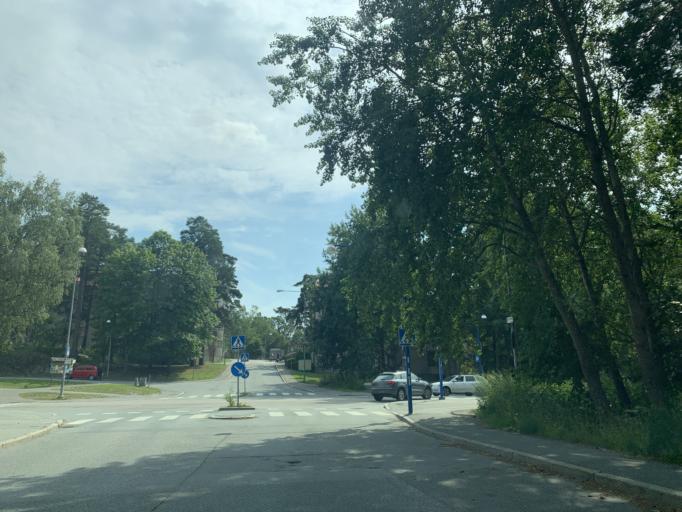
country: SE
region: Stockholm
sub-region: Norrtalje Kommun
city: Bergshamra
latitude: 59.3824
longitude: 18.0290
